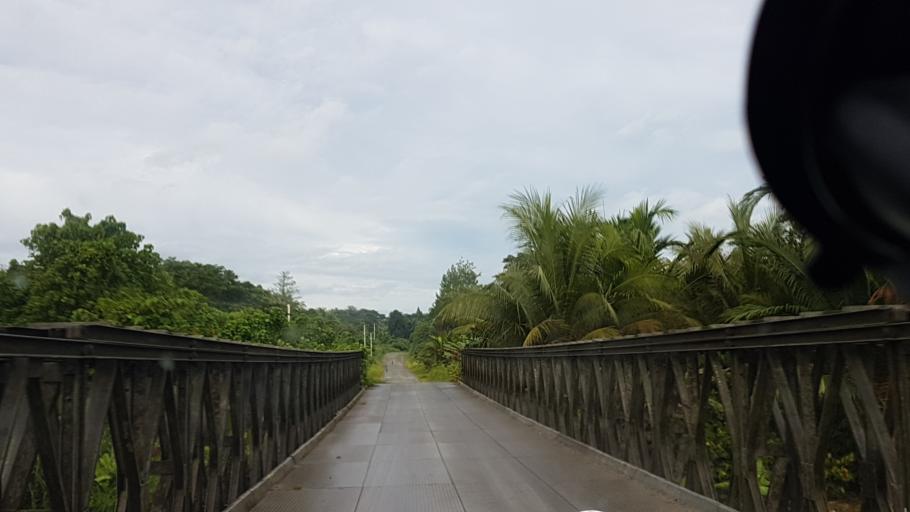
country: PG
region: East Sepik
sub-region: Wewak
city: Wewak
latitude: -3.7011
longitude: 143.2272
